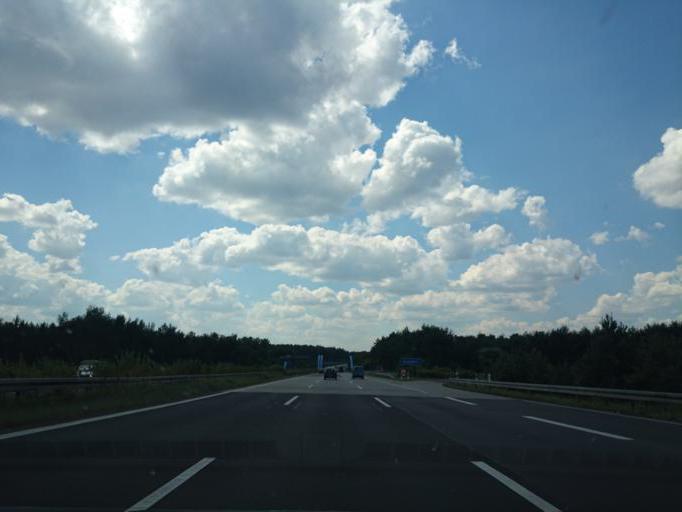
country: DE
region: Berlin
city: Nikolassee
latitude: 52.4023
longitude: 13.1871
